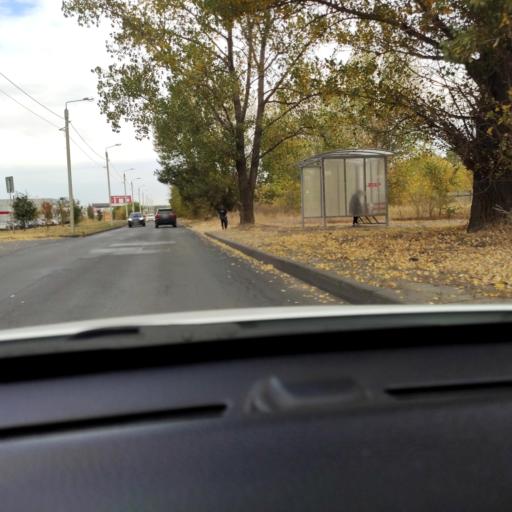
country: RU
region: Voronezj
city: Somovo
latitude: 51.6747
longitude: 39.2912
